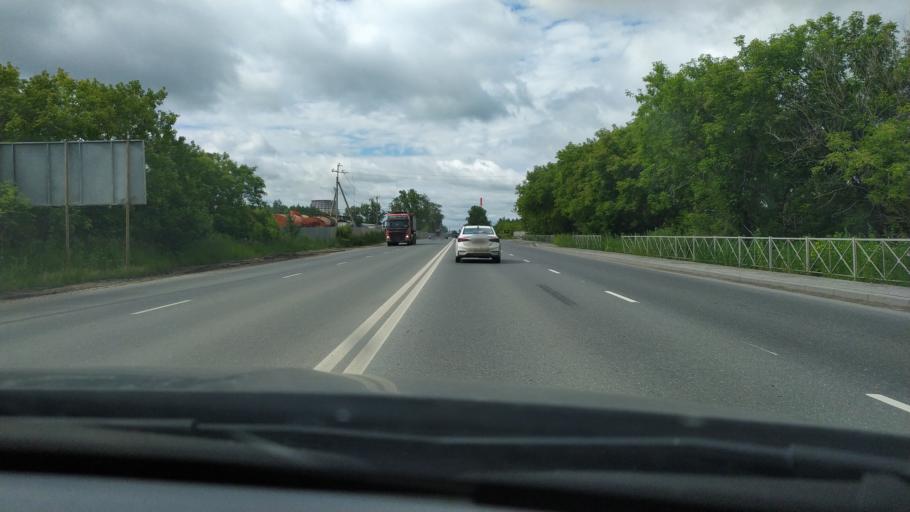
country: RU
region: Perm
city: Kondratovo
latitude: 57.9335
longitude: 56.1530
